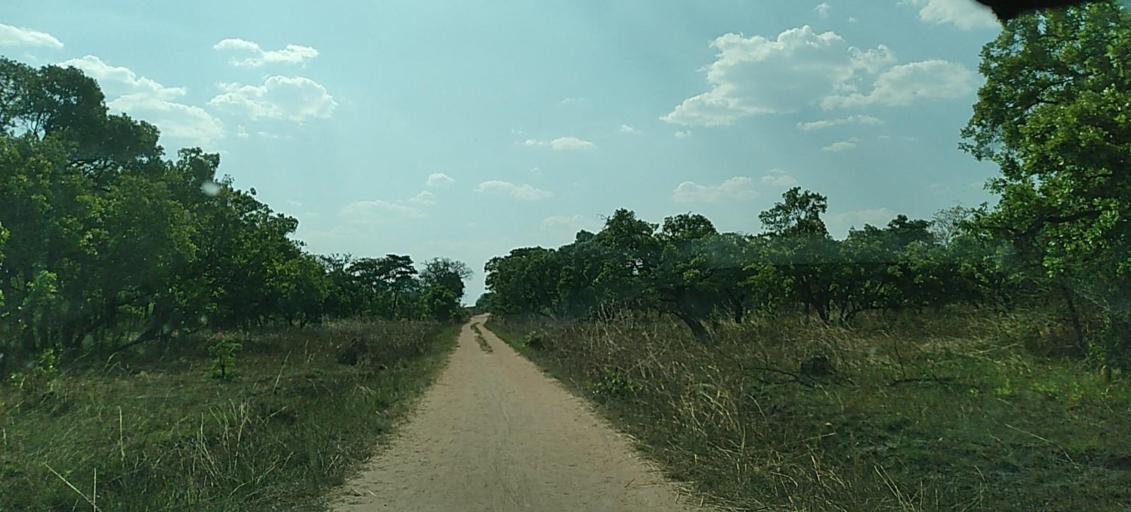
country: ZM
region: North-Western
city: Kalengwa
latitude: -13.1003
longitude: 24.9855
